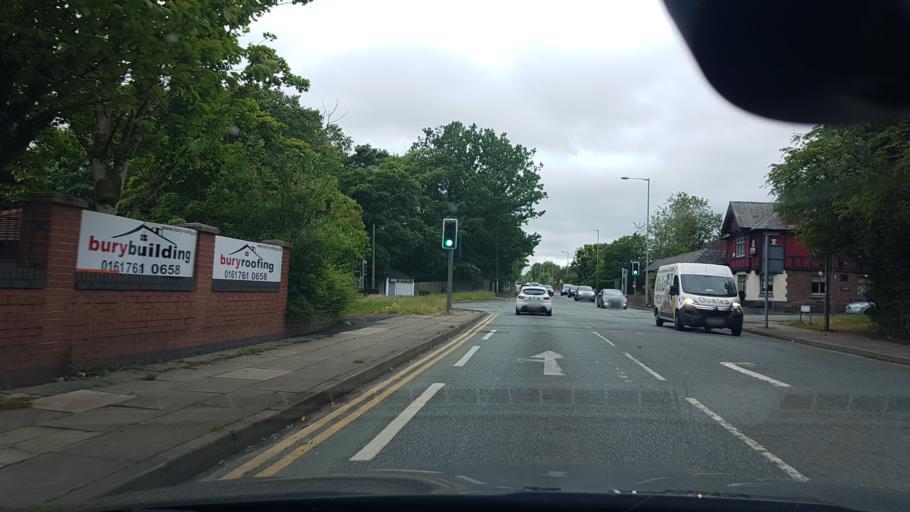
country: GB
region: England
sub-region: Borough of Bury
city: Radcliffe
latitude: 53.5813
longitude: -2.3421
